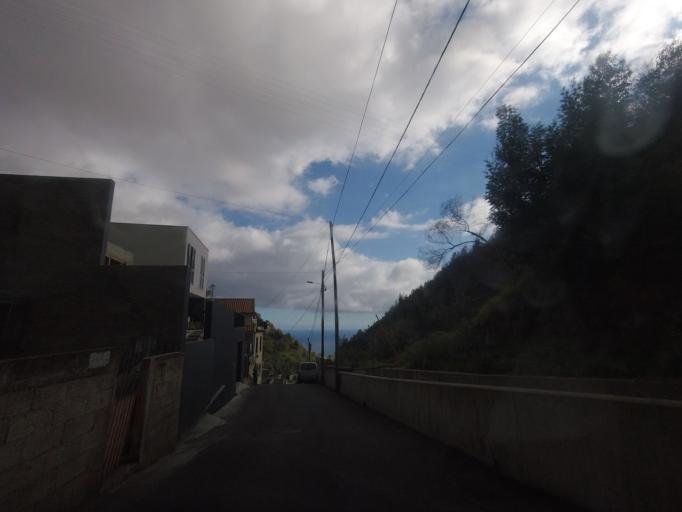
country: PT
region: Madeira
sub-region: Funchal
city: Nossa Senhora do Monte
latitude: 32.6764
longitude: -16.9315
